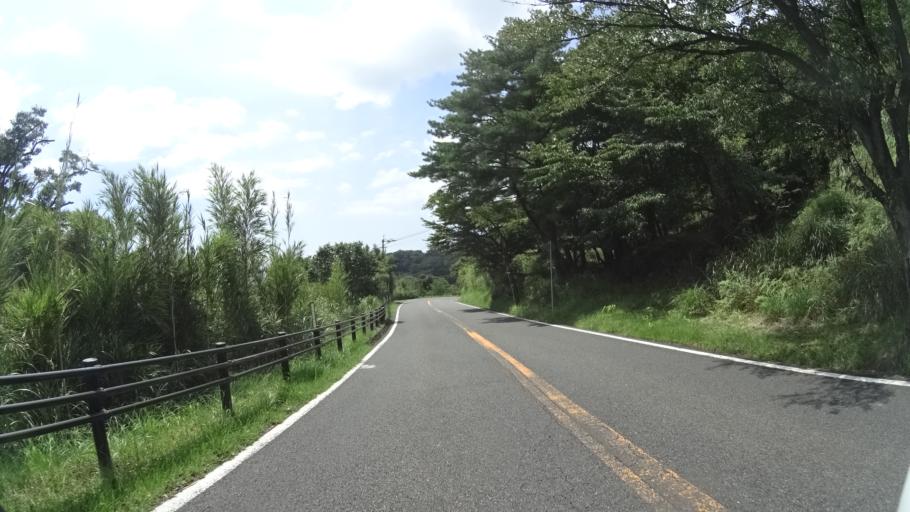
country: JP
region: Miyazaki
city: Kobayashi
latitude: 31.8991
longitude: 130.8371
